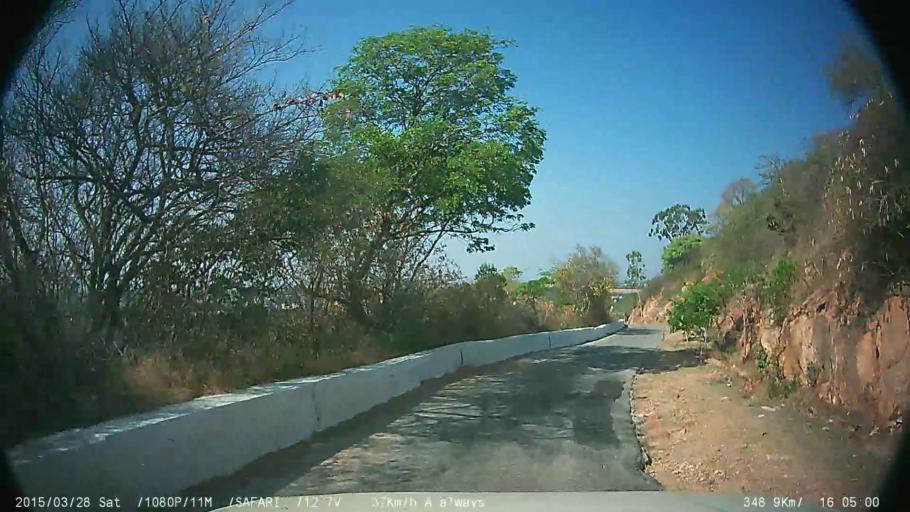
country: IN
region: Karnataka
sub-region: Mysore
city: Mysore
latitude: 12.2839
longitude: 76.6774
